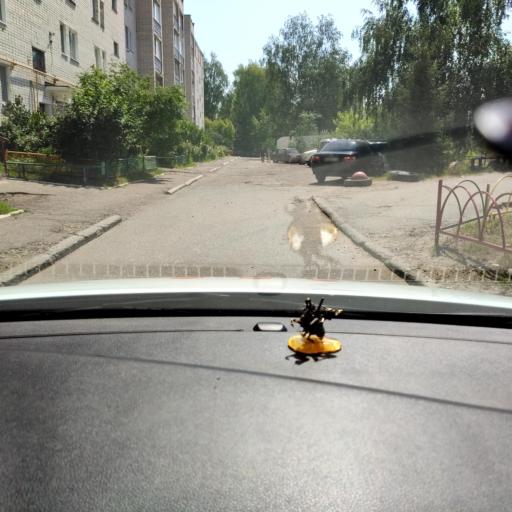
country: RU
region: Tatarstan
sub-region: Zelenodol'skiy Rayon
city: Zelenodolsk
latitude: 55.8531
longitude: 48.5561
